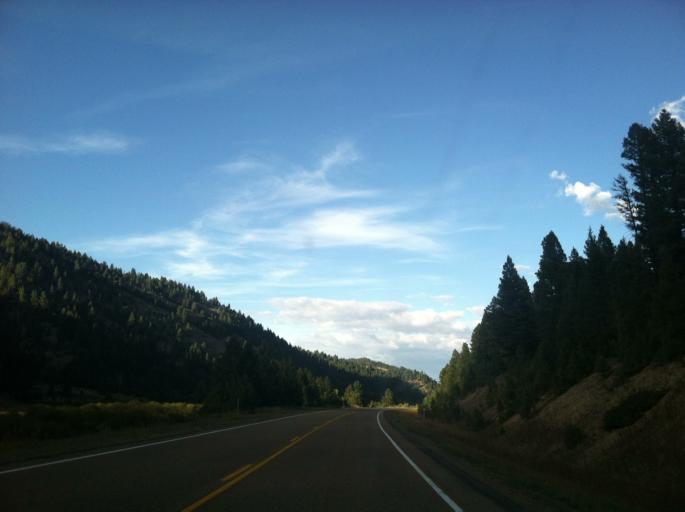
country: US
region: Montana
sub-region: Granite County
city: Philipsburg
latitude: 46.4301
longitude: -113.2723
